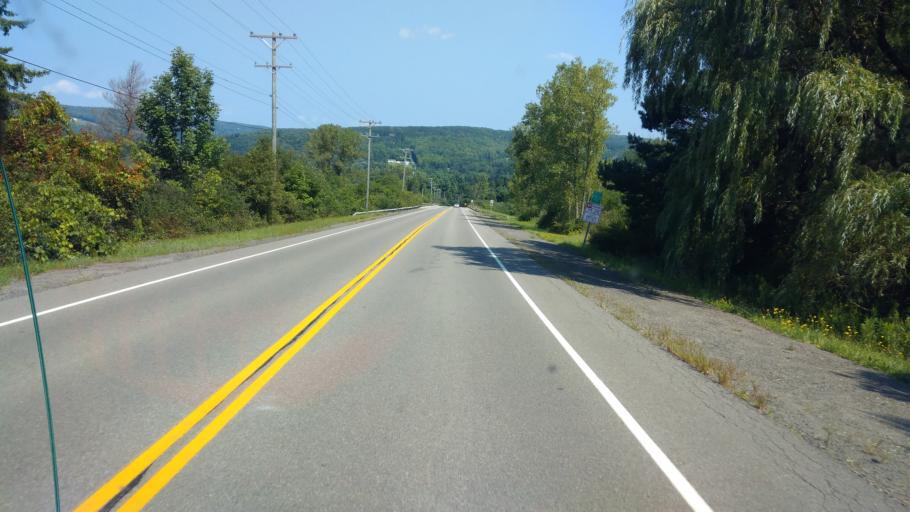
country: US
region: New York
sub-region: Allegany County
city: Belmont
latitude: 42.2968
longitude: -78.0262
